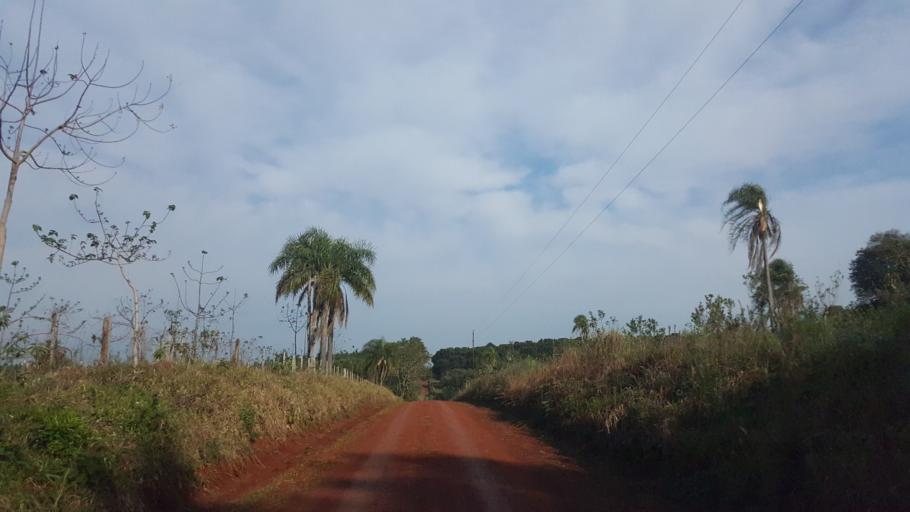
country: AR
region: Misiones
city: Capiovi
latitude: -26.8938
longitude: -55.0989
